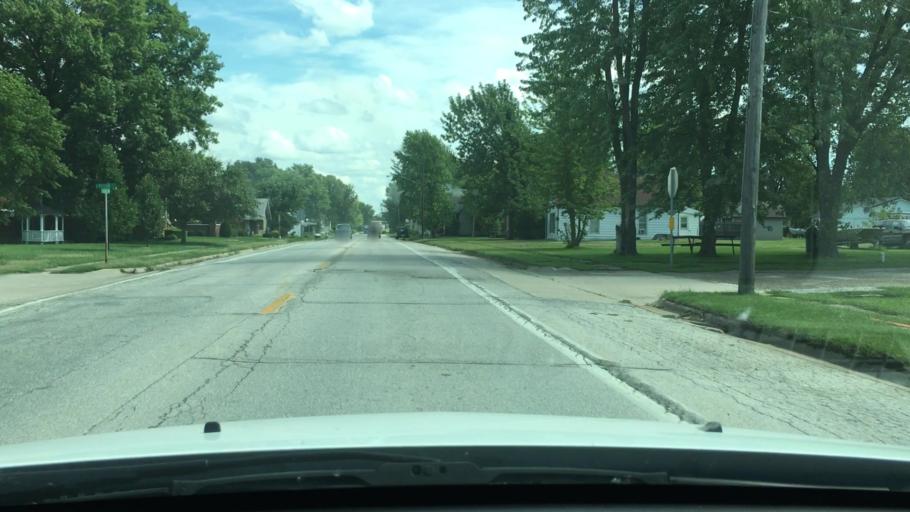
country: US
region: Missouri
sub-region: Audrain County
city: Vandalia
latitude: 39.3119
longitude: -91.4857
